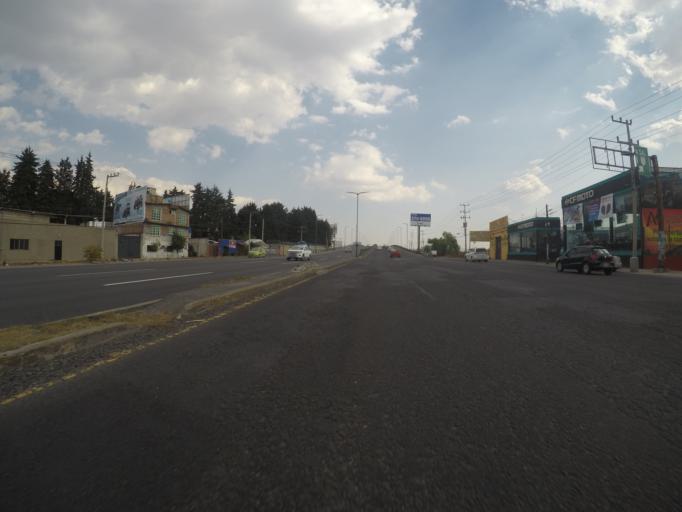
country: MX
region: Morelos
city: San Miguel Totocuitlapilco
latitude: 19.2383
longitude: -99.5989
